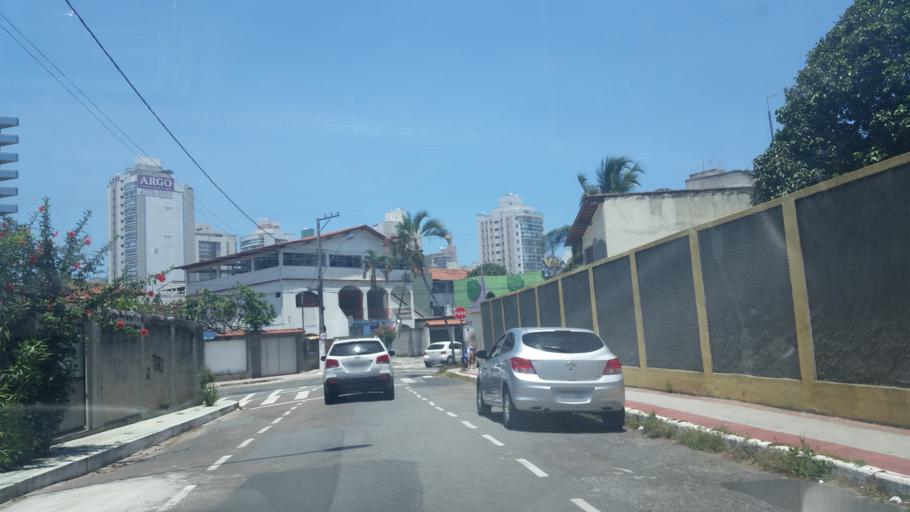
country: BR
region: Espirito Santo
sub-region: Vila Velha
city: Vila Velha
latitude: -20.3382
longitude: -40.2888
